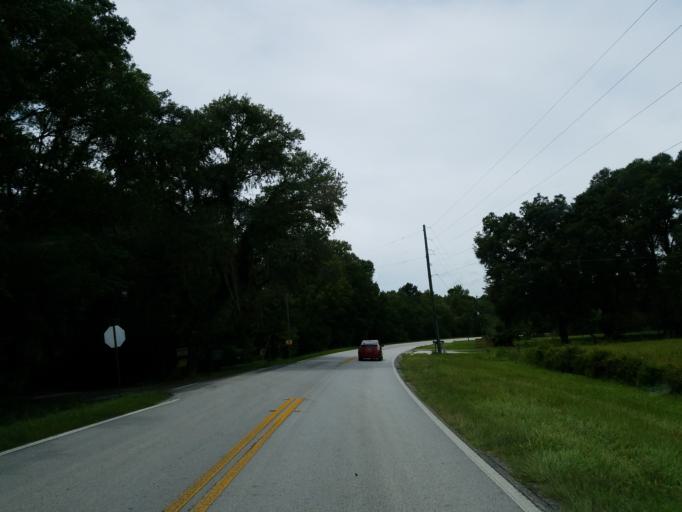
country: US
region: Florida
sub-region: Sumter County
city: Bushnell
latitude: 28.6691
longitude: -82.1843
